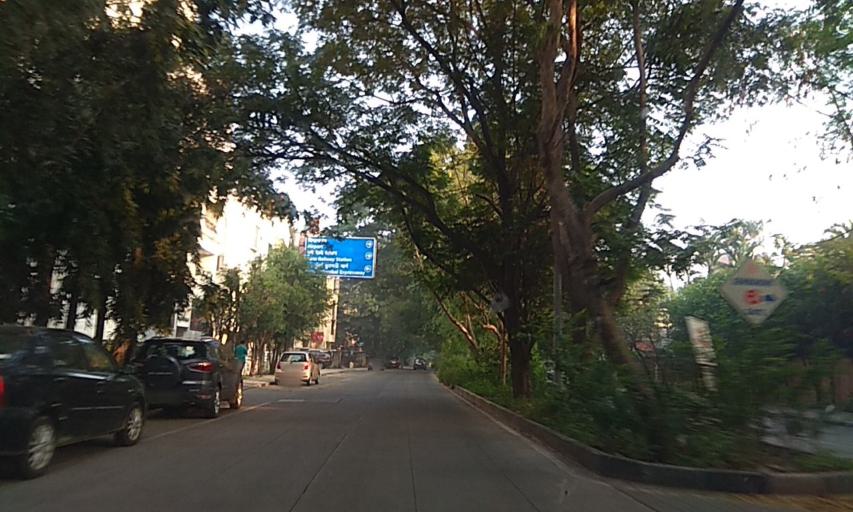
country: IN
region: Maharashtra
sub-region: Pune Division
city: Shivaji Nagar
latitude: 18.5453
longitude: 73.8171
